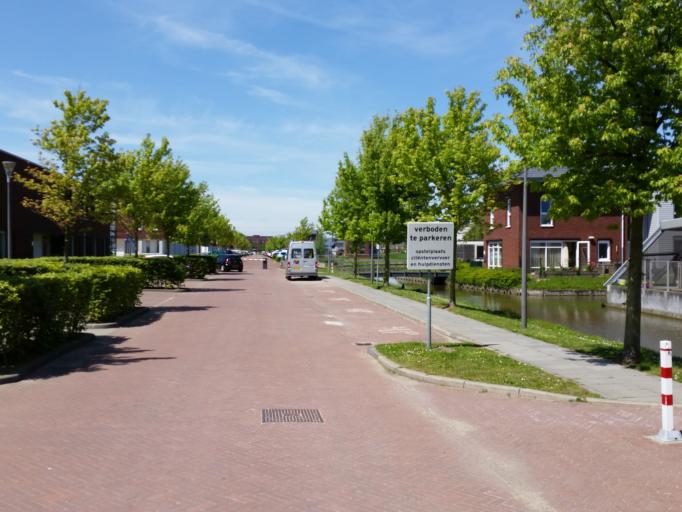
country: NL
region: South Holland
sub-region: Gemeente Den Haag
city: Ypenburg
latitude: 52.0389
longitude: 4.3807
